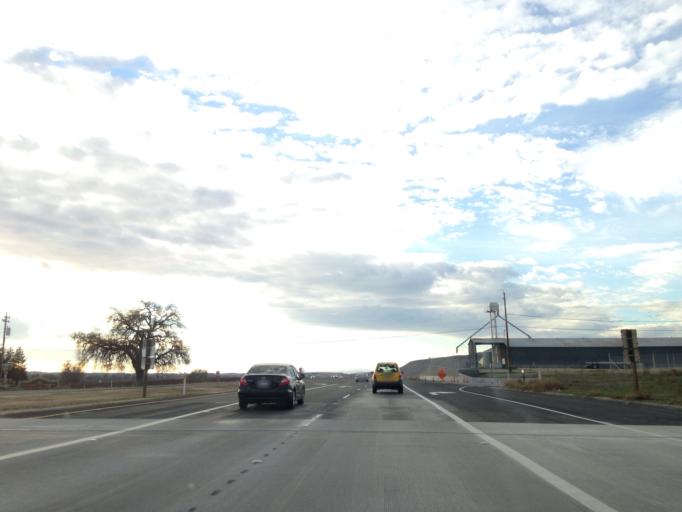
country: US
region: California
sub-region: San Luis Obispo County
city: Shandon
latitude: 35.6617
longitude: -120.4132
